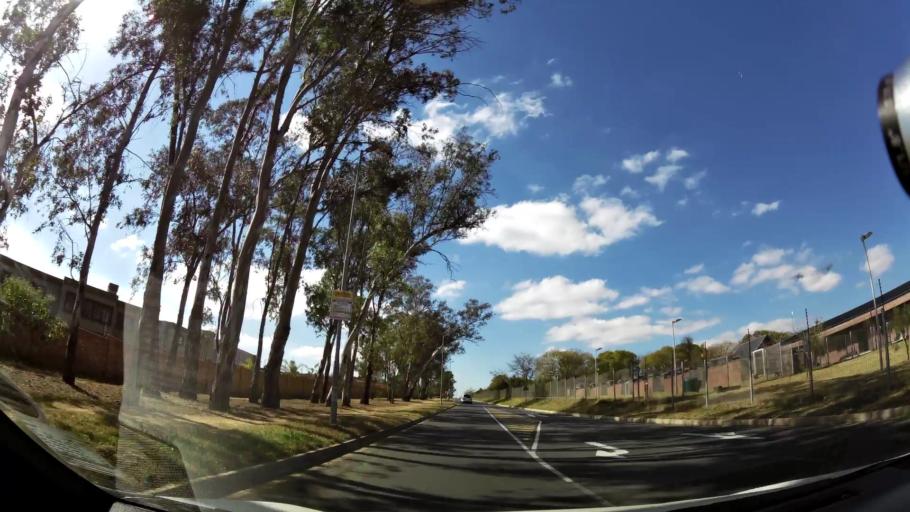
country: ZA
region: Gauteng
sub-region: City of Johannesburg Metropolitan Municipality
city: Midrand
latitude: -25.9965
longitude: 28.0944
